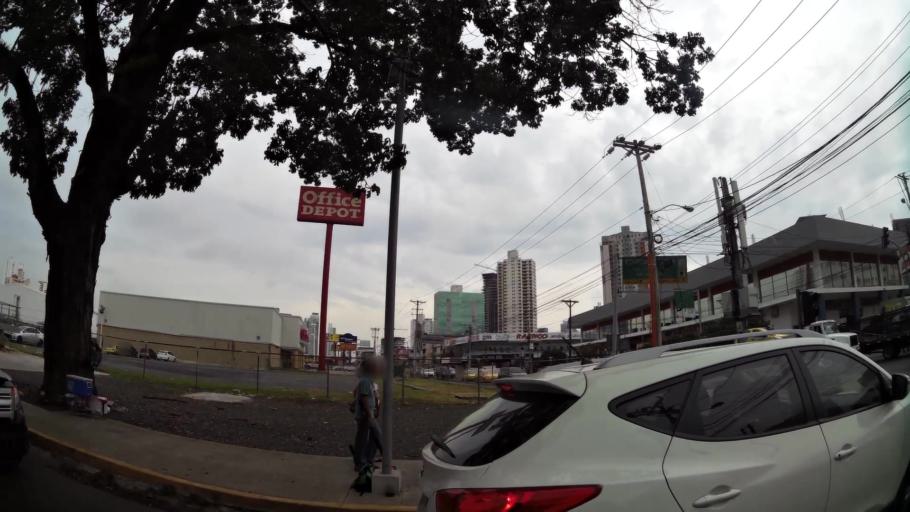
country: PA
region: Panama
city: Panama
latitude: 8.9916
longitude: -79.5209
